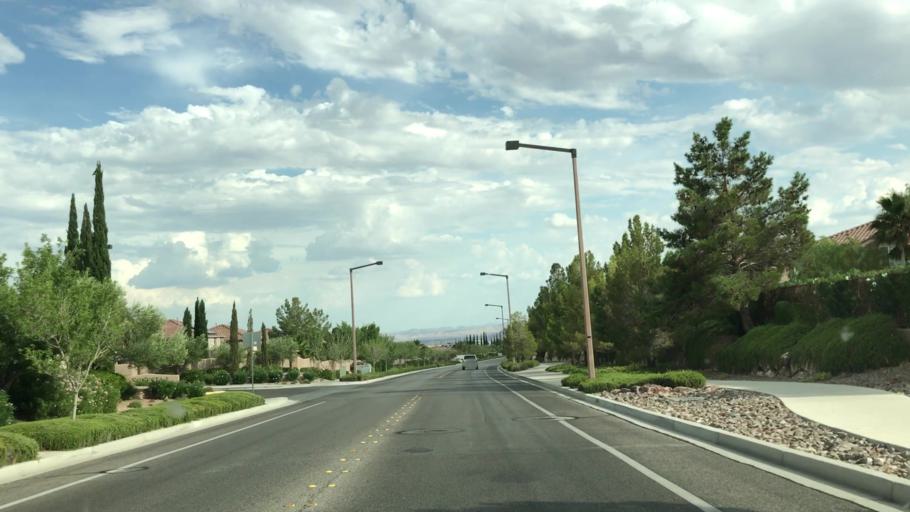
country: US
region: Nevada
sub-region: Clark County
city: Summerlin South
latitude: 36.1706
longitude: -115.3513
